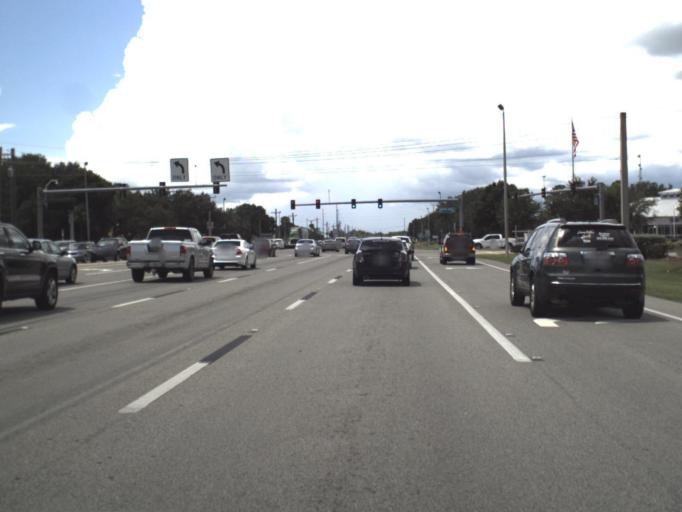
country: US
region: Florida
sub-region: Charlotte County
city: Port Charlotte
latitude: 27.0102
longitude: -82.1399
